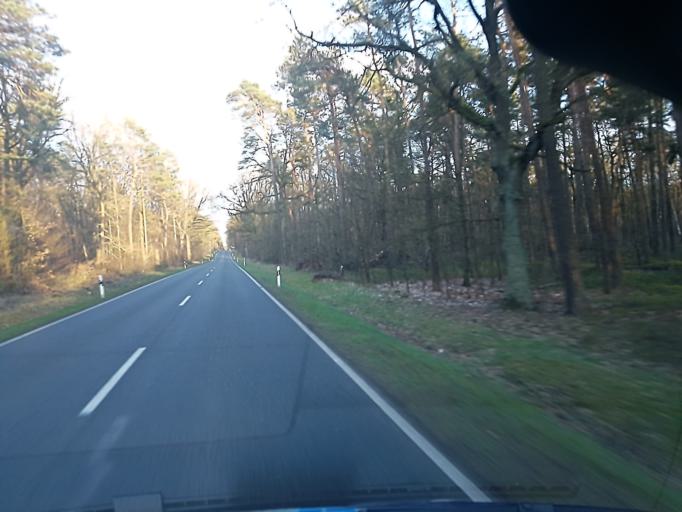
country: DE
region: Saxony
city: Doberschutz
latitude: 51.5681
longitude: 12.7591
